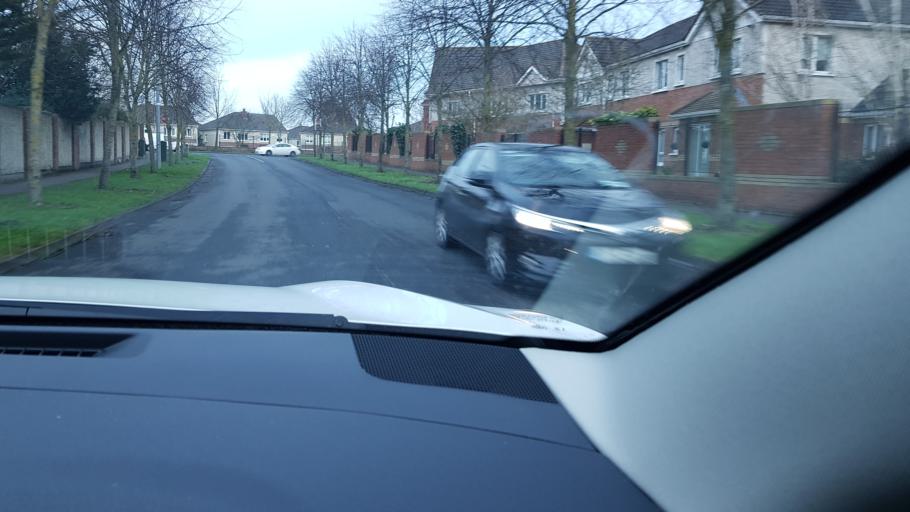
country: IE
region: Leinster
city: Hartstown
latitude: 53.4003
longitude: -6.4353
